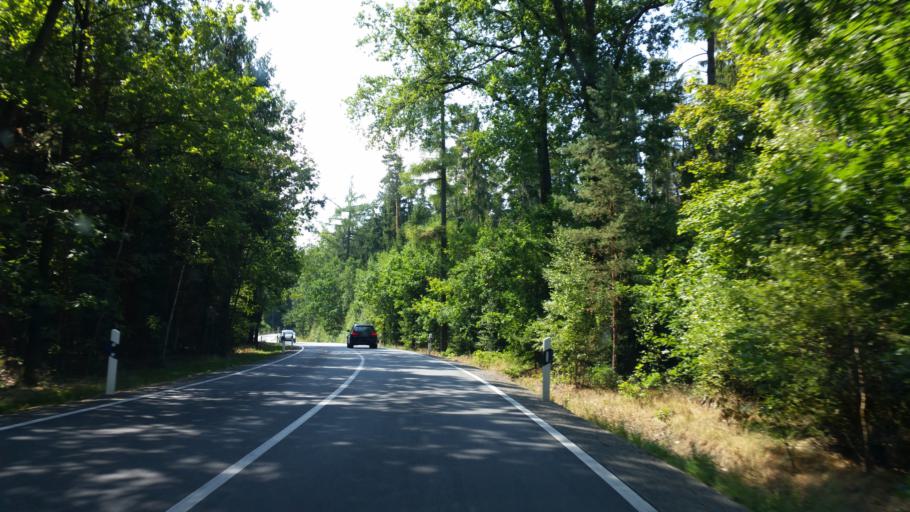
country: DE
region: Saxony
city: Grosshennersdorf
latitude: 50.9766
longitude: 14.7541
